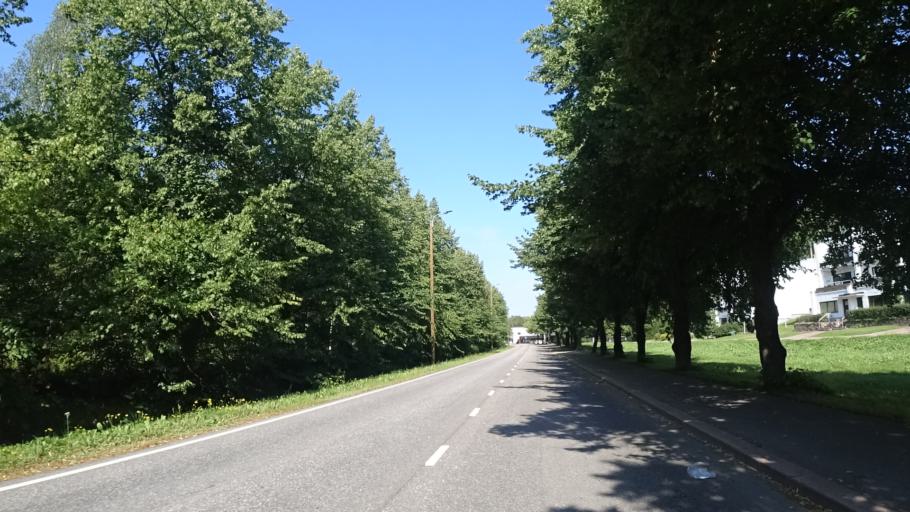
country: FI
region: Kymenlaakso
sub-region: Kotka-Hamina
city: Karhula
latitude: 60.4994
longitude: 26.9545
